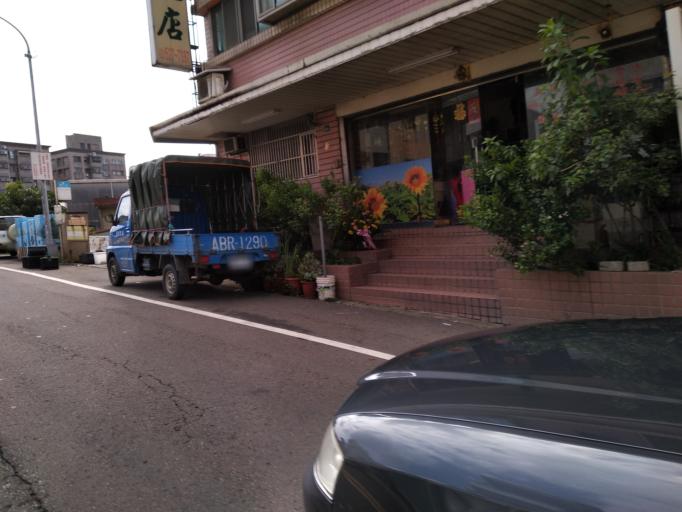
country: TW
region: Taiwan
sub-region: Hsinchu
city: Hsinchu
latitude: 24.7975
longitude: 120.9561
